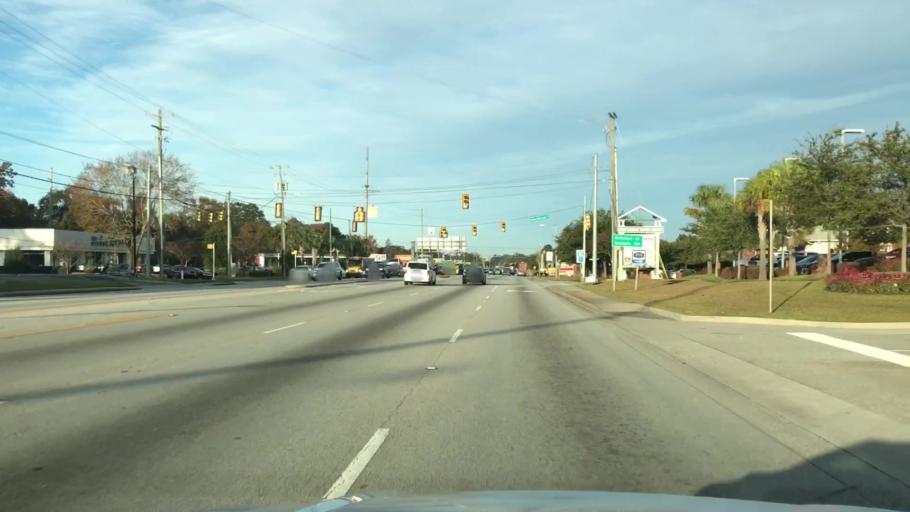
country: US
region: South Carolina
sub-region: Charleston County
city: Shell Point
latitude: 32.7909
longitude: -80.0358
